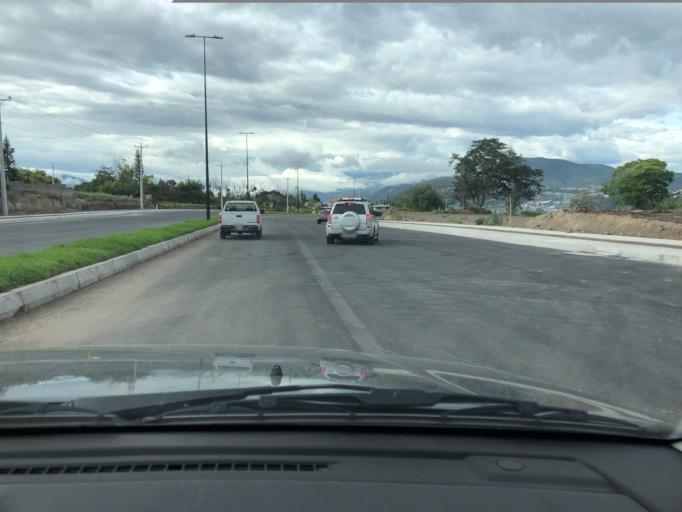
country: EC
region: Imbabura
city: Ibarra
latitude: 0.3377
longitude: -78.1569
